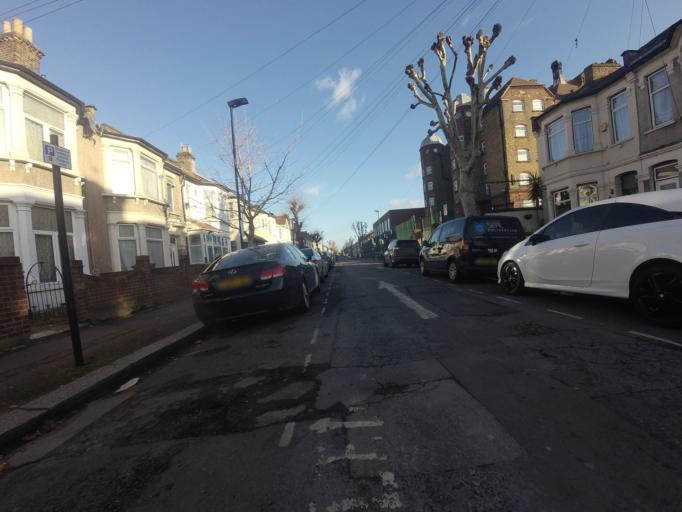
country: GB
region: England
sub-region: Greater London
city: East Ham
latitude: 51.5380
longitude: 0.0525
